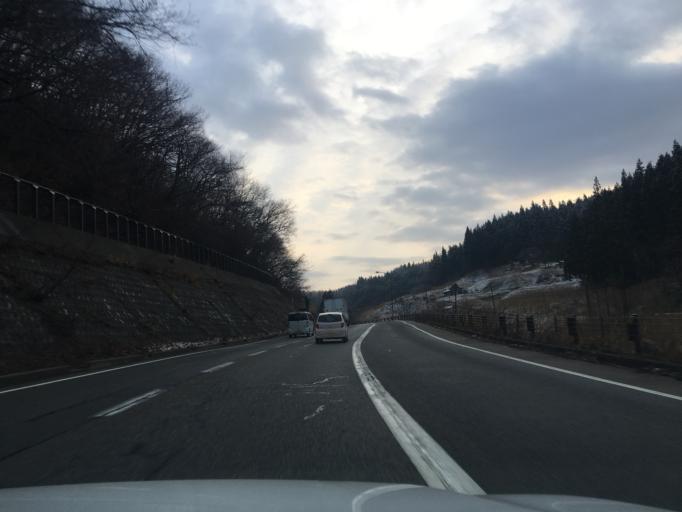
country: JP
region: Niigata
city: Murakami
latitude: 38.4227
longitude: 139.5687
